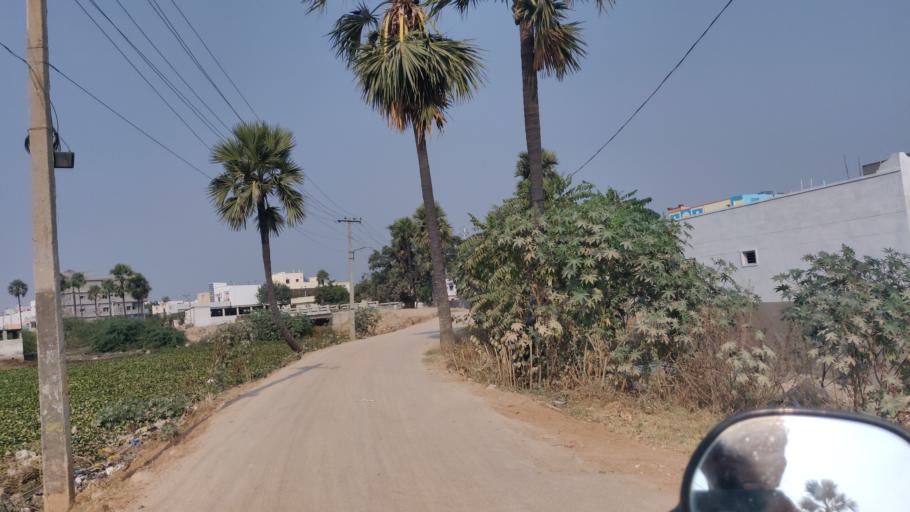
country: IN
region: Telangana
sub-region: Rangareddi
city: Uppal Kalan
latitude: 17.3933
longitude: 78.6045
